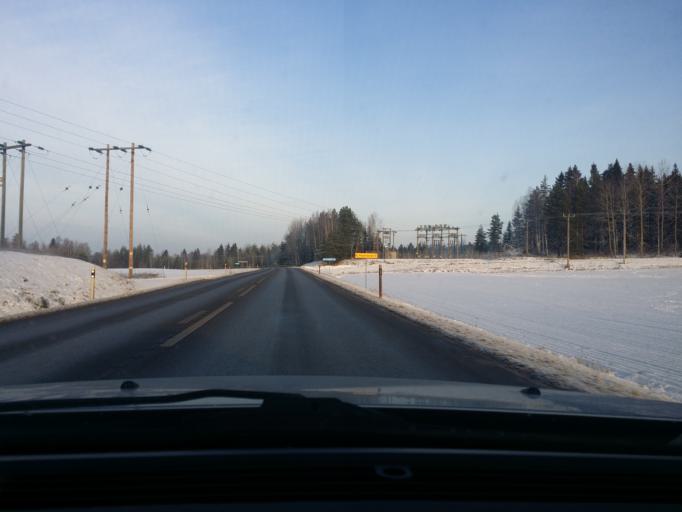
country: SE
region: OErebro
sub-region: Lindesbergs Kommun
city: Frovi
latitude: 59.5014
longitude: 15.3751
